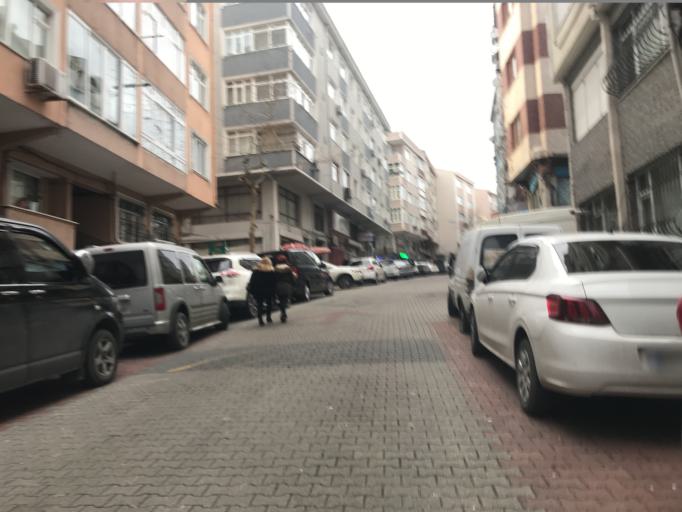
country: TR
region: Istanbul
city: Istanbul
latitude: 41.0226
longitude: 28.9422
